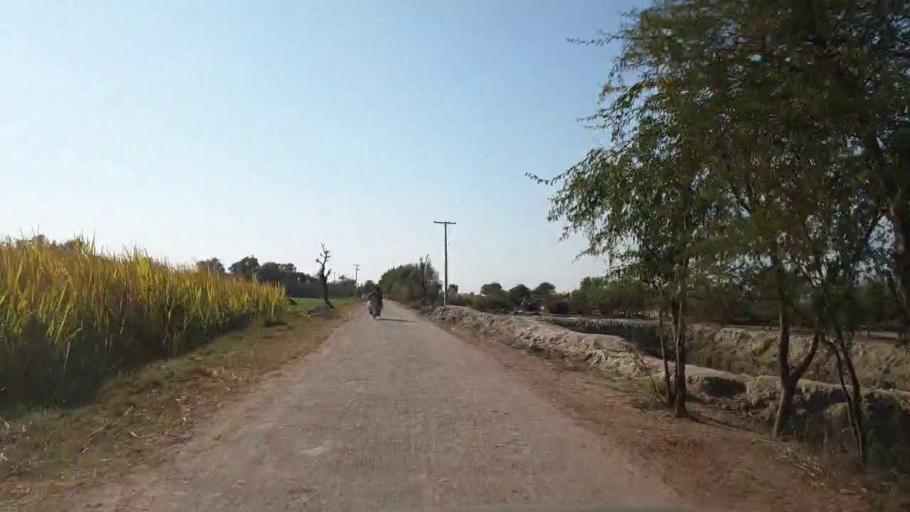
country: PK
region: Sindh
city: Khadro
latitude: 26.1557
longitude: 68.7766
